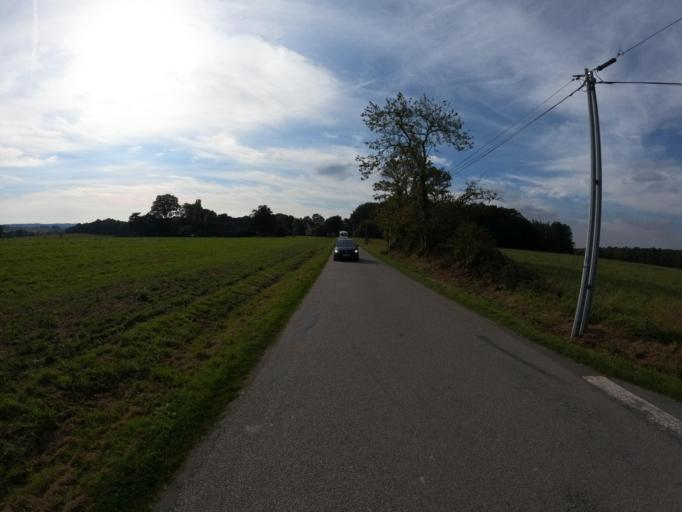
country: FR
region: Brittany
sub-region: Departement du Morbihan
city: Ploermel
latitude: 47.8805
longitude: -2.3966
